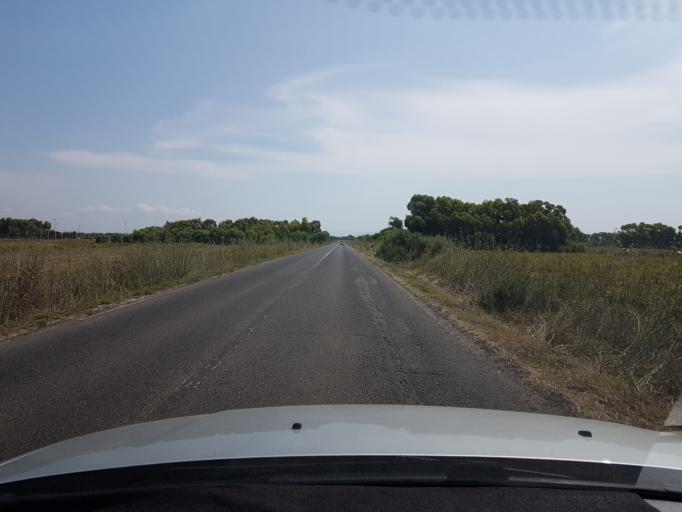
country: IT
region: Sardinia
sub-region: Provincia di Oristano
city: Cabras
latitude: 39.9163
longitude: 8.4827
